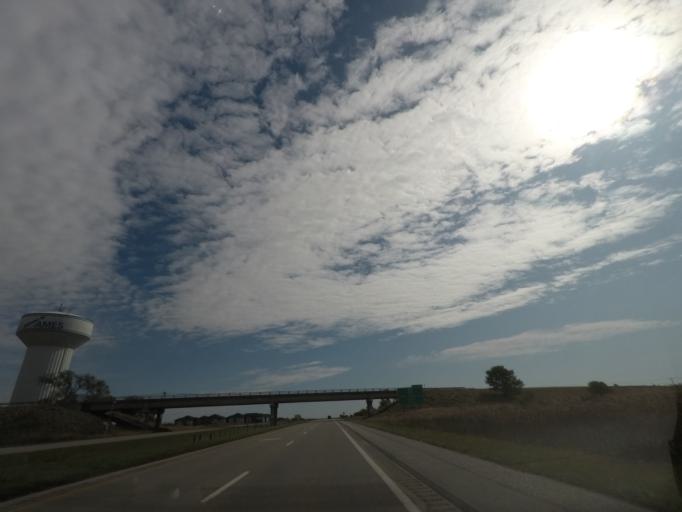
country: US
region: Iowa
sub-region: Story County
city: Ames
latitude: 42.0147
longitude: -93.6999
